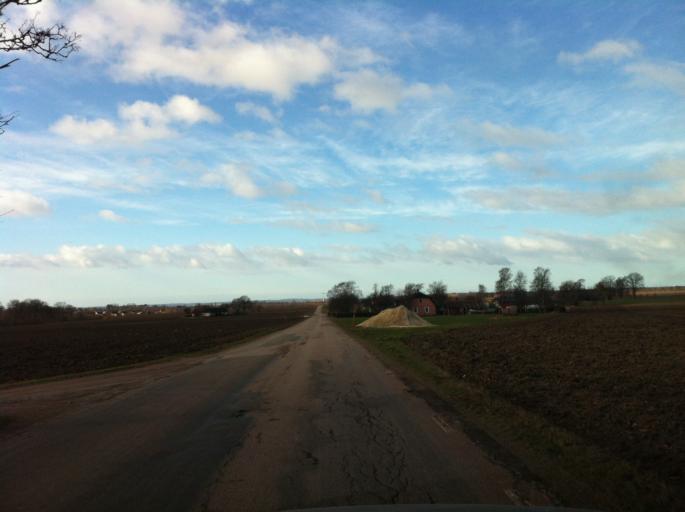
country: SE
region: Skane
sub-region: Helsingborg
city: Barslov
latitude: 55.9880
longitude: 12.8368
